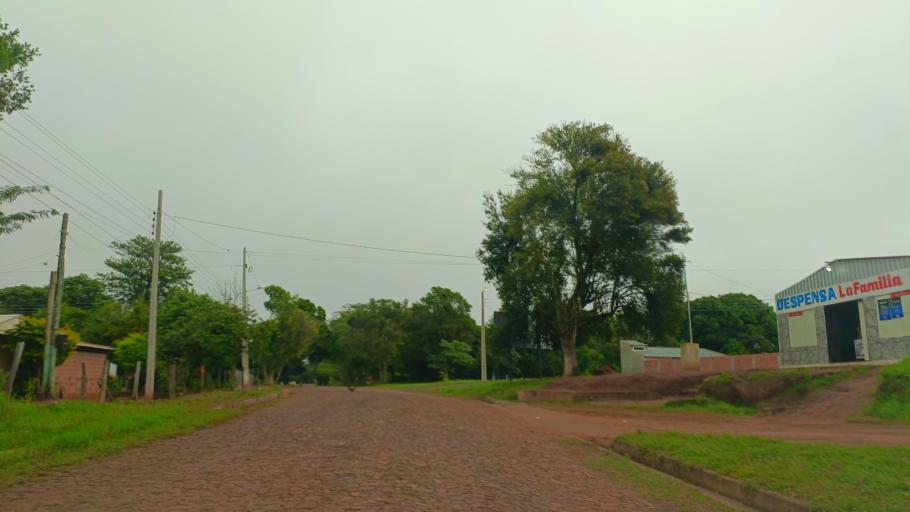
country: PY
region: Misiones
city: Santa Maria
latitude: -26.8611
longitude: -57.0307
